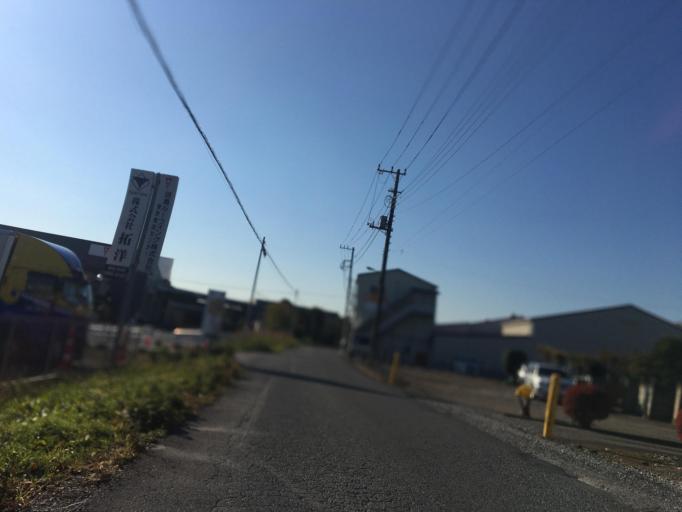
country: JP
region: Saitama
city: Yashio-shi
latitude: 35.8083
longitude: 139.8232
